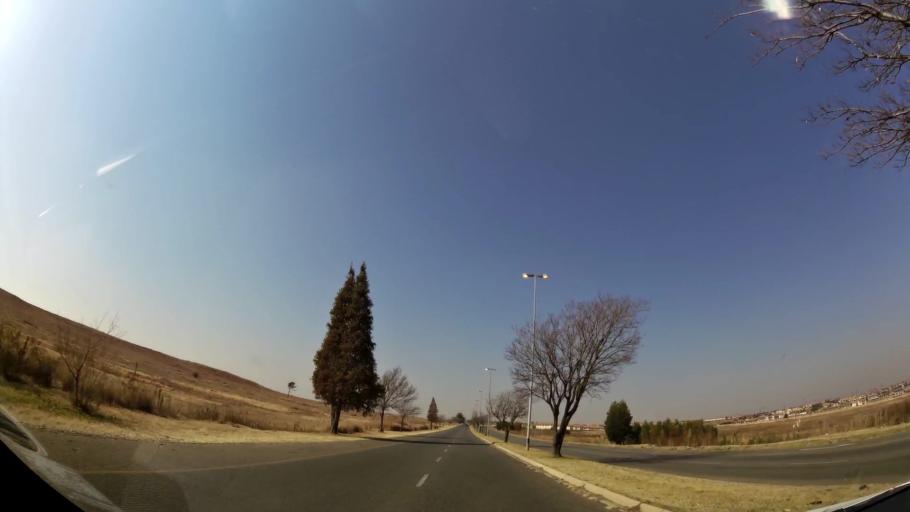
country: ZA
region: Gauteng
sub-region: Ekurhuleni Metropolitan Municipality
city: Boksburg
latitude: -26.2360
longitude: 28.2820
